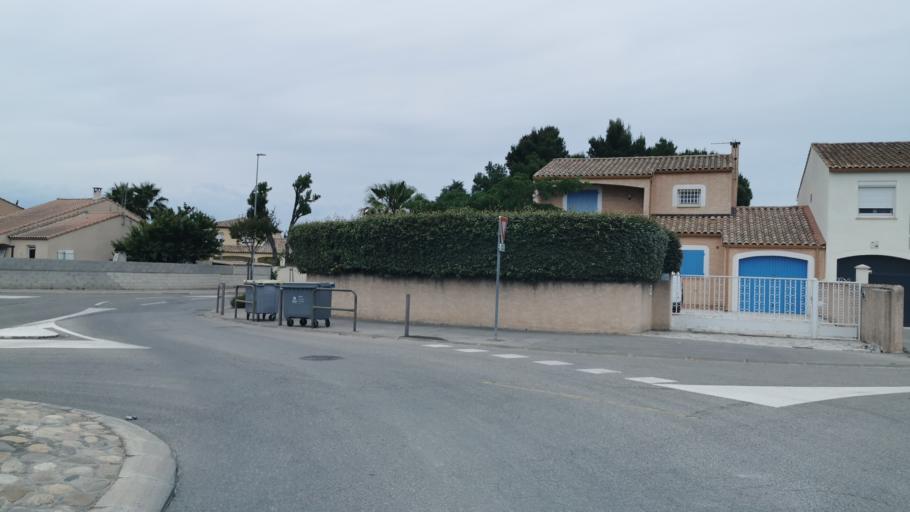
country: FR
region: Languedoc-Roussillon
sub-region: Departement de l'Aude
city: Narbonne
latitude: 43.1947
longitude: 3.0217
